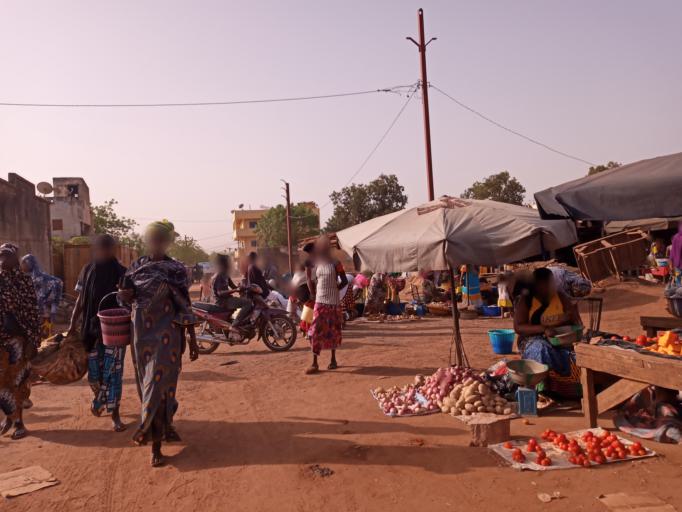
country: ML
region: Bamako
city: Bamako
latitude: 12.6565
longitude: -7.9894
